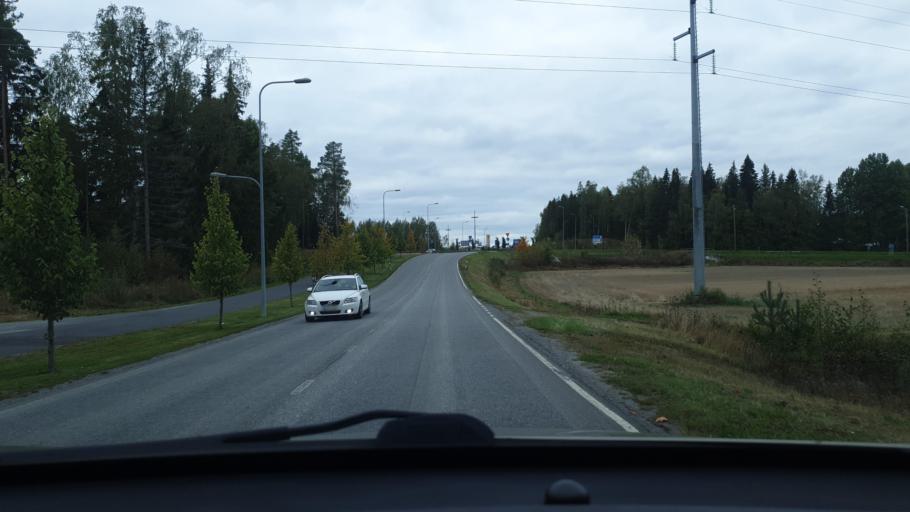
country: FI
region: Ostrobothnia
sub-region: Vaasa
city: Korsholm
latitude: 63.1086
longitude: 21.6674
